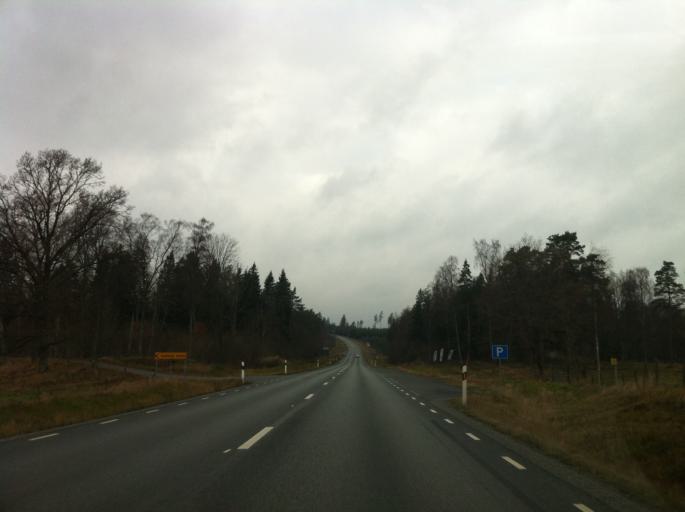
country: SE
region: Joenkoeping
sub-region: Savsjo Kommun
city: Saevsjoe
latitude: 57.3913
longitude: 14.7709
